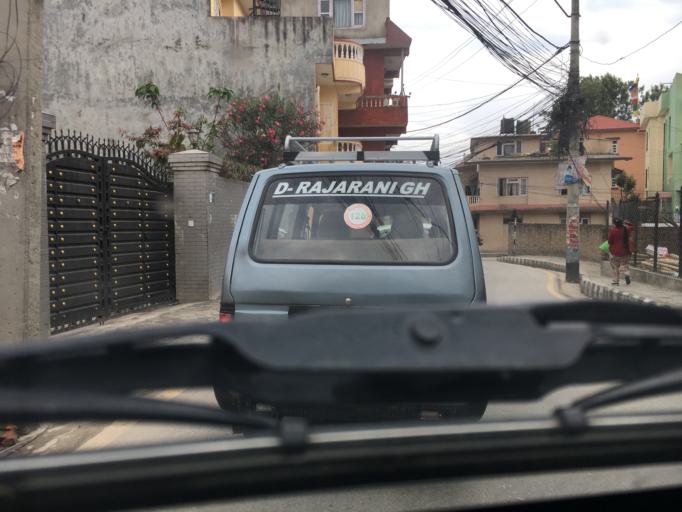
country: NP
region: Central Region
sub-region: Bagmati Zone
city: Kathmandu
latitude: 27.7389
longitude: 85.3491
